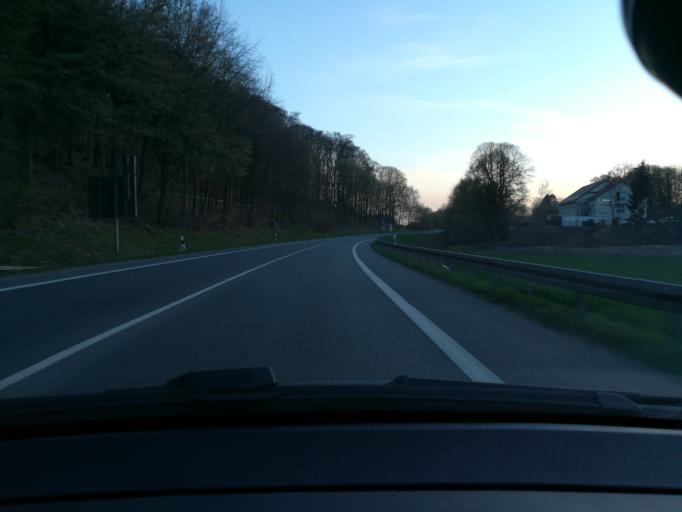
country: DE
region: North Rhine-Westphalia
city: Halle
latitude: 52.0734
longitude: 8.3667
